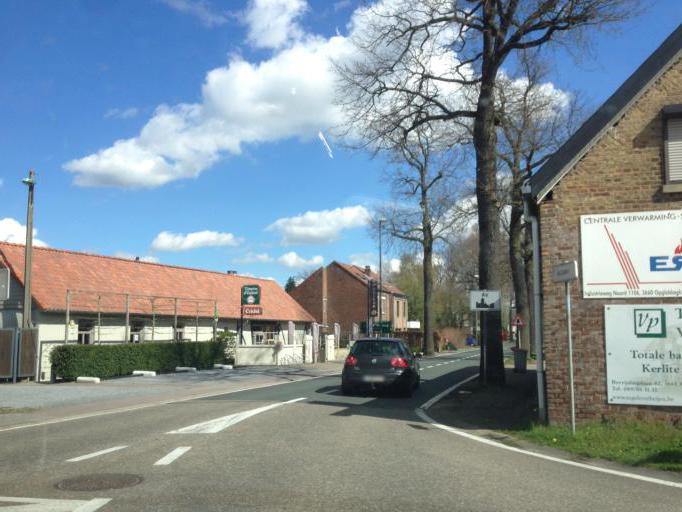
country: BE
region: Flanders
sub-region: Provincie Limburg
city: As
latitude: 50.9997
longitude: 5.5777
